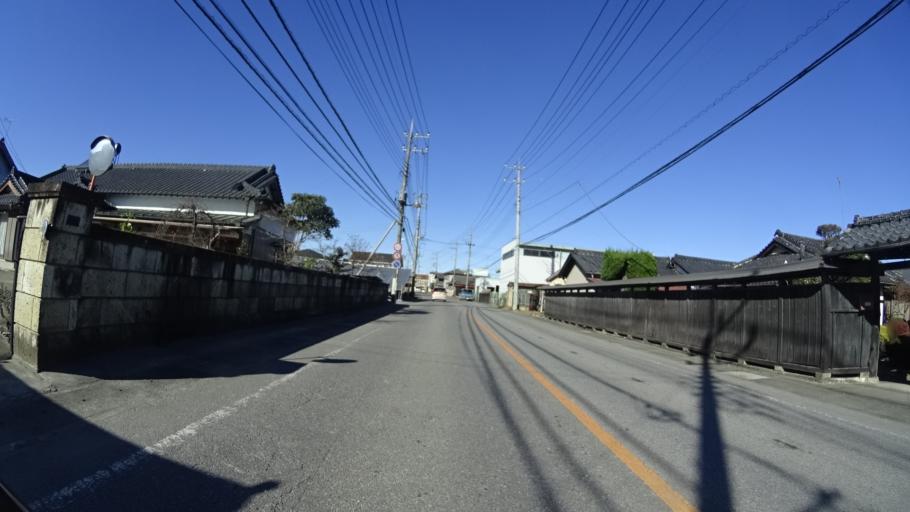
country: JP
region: Tochigi
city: Mibu
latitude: 36.4650
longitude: 139.7514
